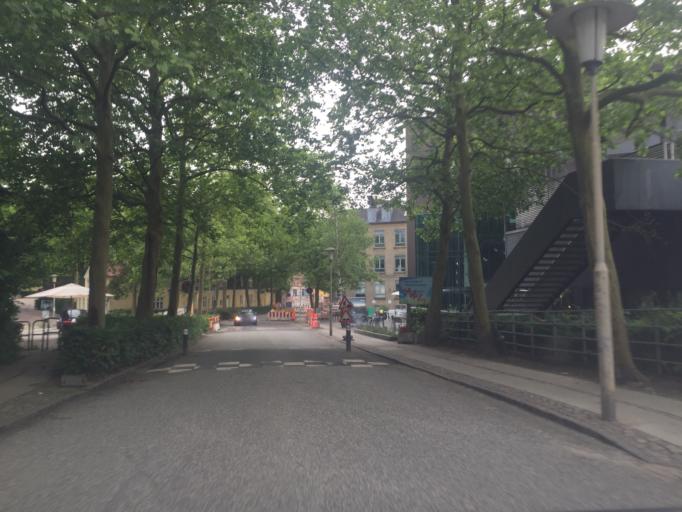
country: DK
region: Capital Region
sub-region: Lyngby-Tarbaek Kommune
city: Kongens Lyngby
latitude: 55.7751
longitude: 12.5018
